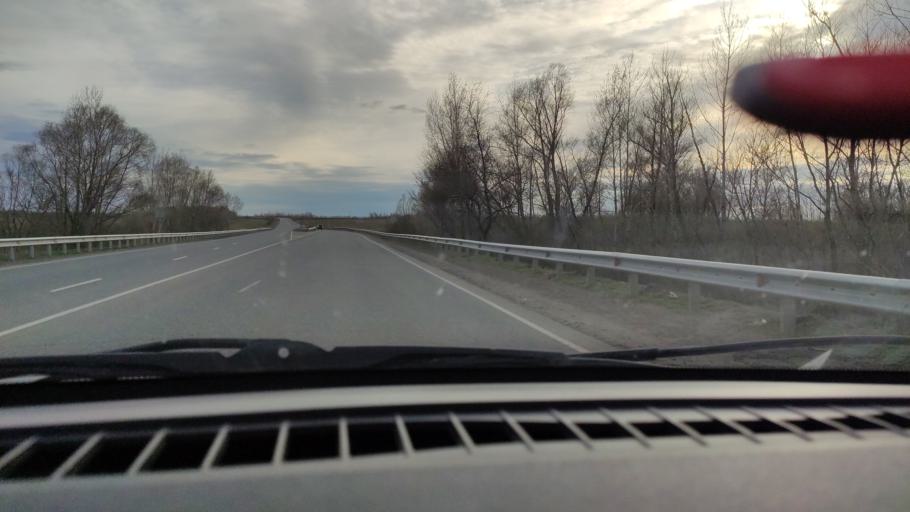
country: RU
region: Orenburg
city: Tatarskaya Kargala
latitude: 52.0227
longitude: 55.2193
